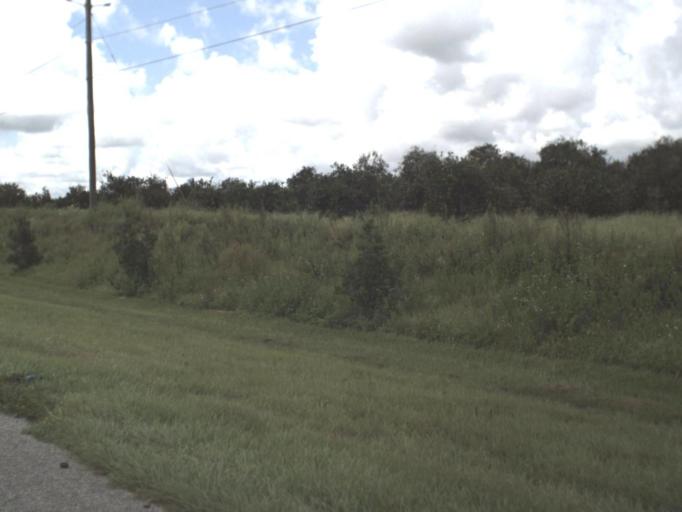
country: US
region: Florida
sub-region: Hardee County
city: Wauchula
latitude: 27.5211
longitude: -81.8093
